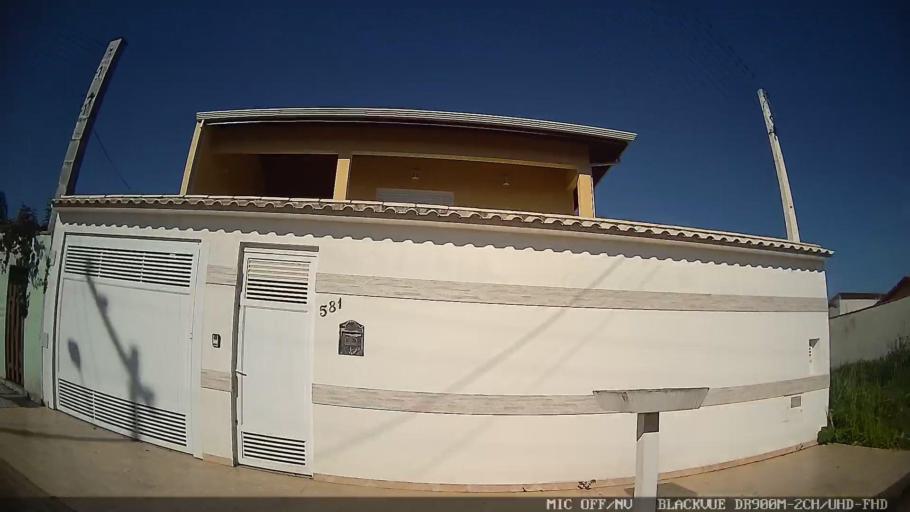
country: BR
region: Sao Paulo
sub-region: Peruibe
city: Peruibe
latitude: -24.2796
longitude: -46.9499
